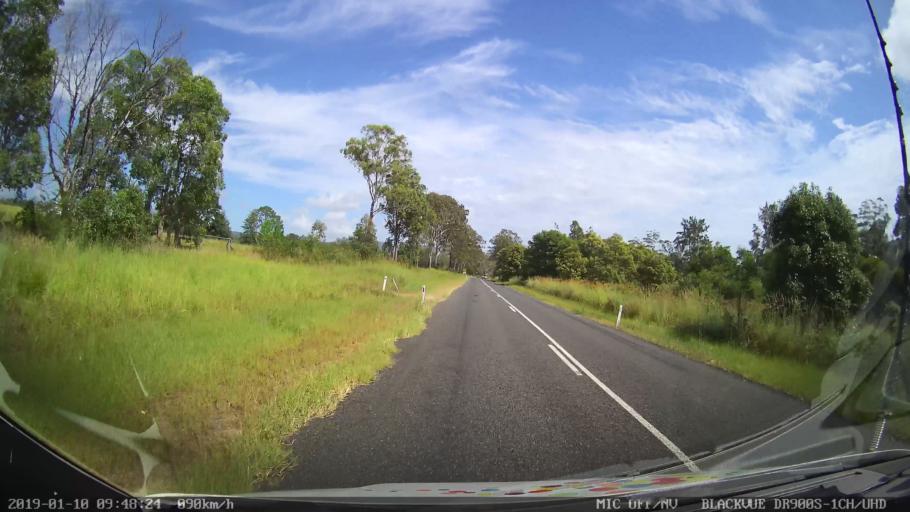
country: AU
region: New South Wales
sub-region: Coffs Harbour
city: Nana Glen
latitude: -30.0730
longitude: 152.9878
